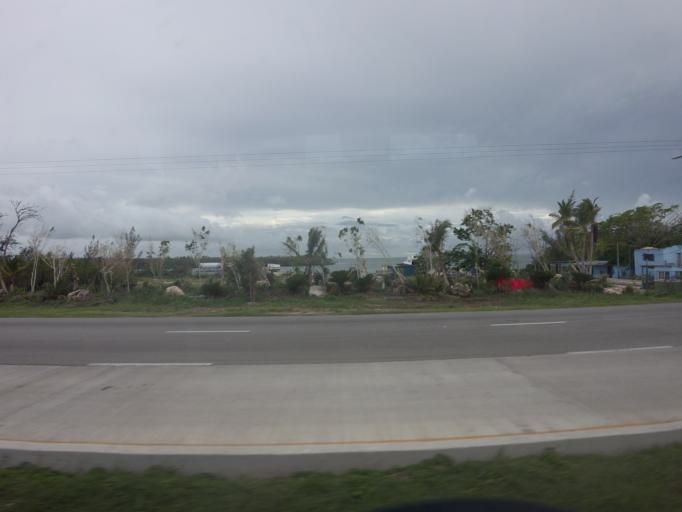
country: CU
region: Matanzas
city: Varadero
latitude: 23.1796
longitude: -81.1945
